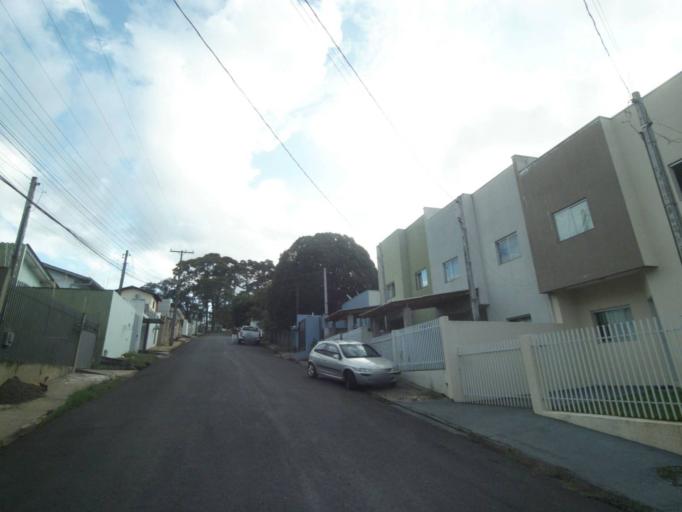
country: BR
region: Parana
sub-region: Telemaco Borba
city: Telemaco Borba
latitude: -24.3299
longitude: -50.6090
